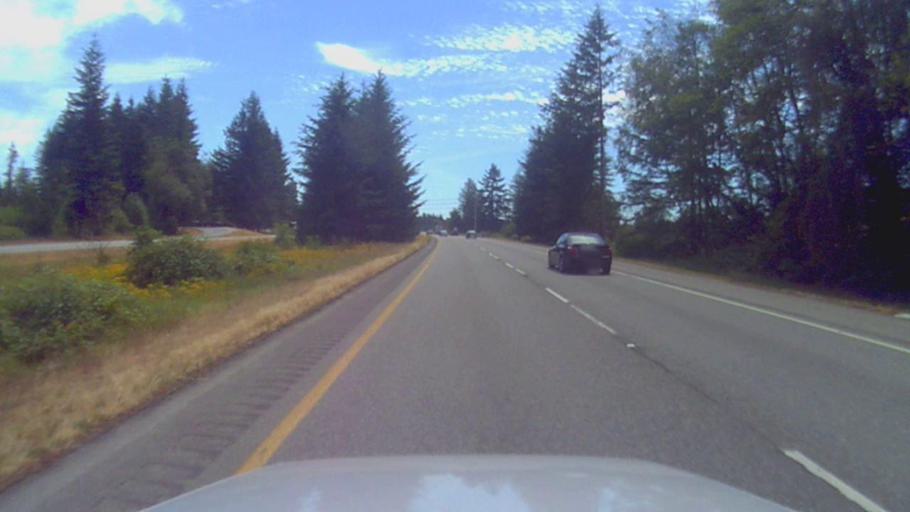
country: US
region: Washington
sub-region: Whatcom County
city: Ferndale
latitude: 48.9104
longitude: -122.6259
